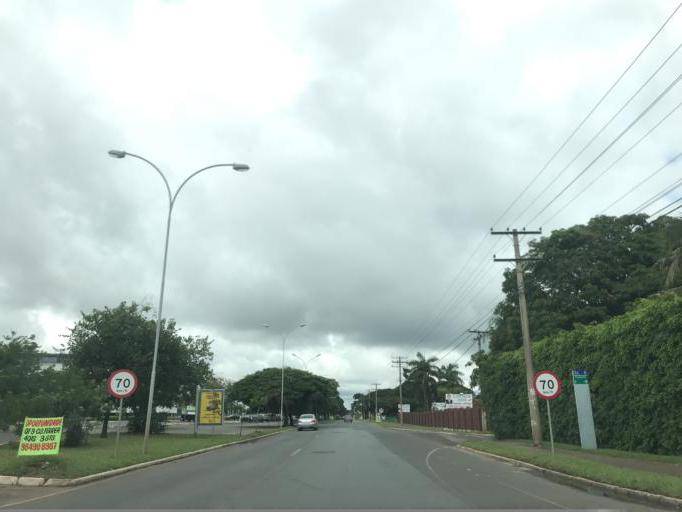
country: BR
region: Federal District
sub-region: Brasilia
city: Brasilia
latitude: -15.8445
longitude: -47.8933
